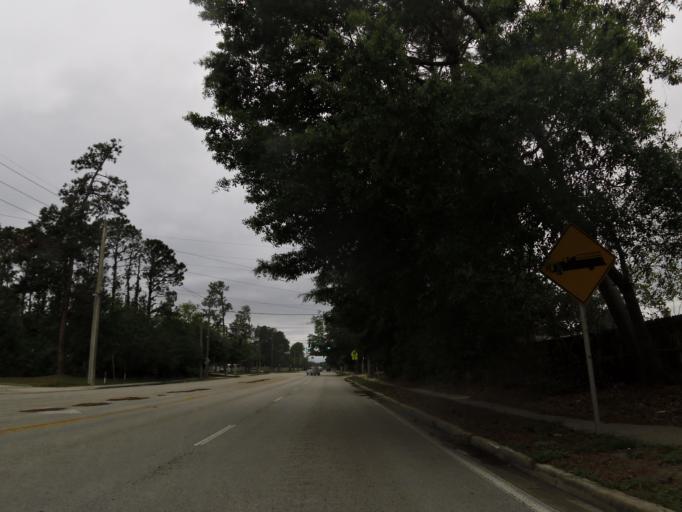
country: US
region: Florida
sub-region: Saint Johns County
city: Fruit Cove
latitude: 30.1951
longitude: -81.6118
